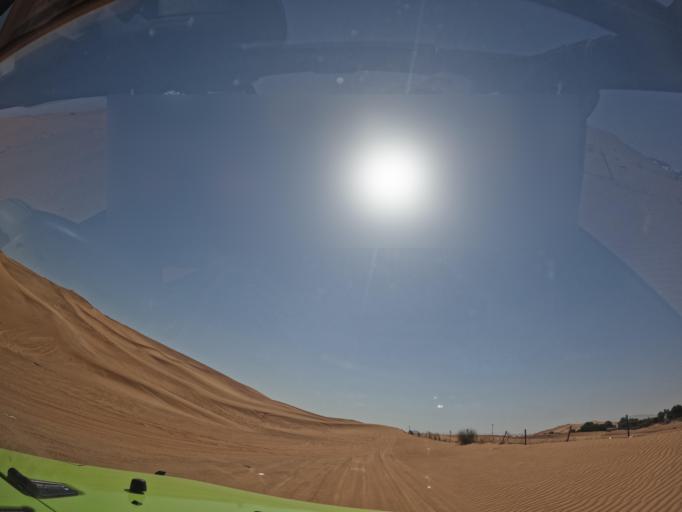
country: AE
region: Ash Shariqah
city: Adh Dhayd
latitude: 24.9594
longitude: 55.7145
